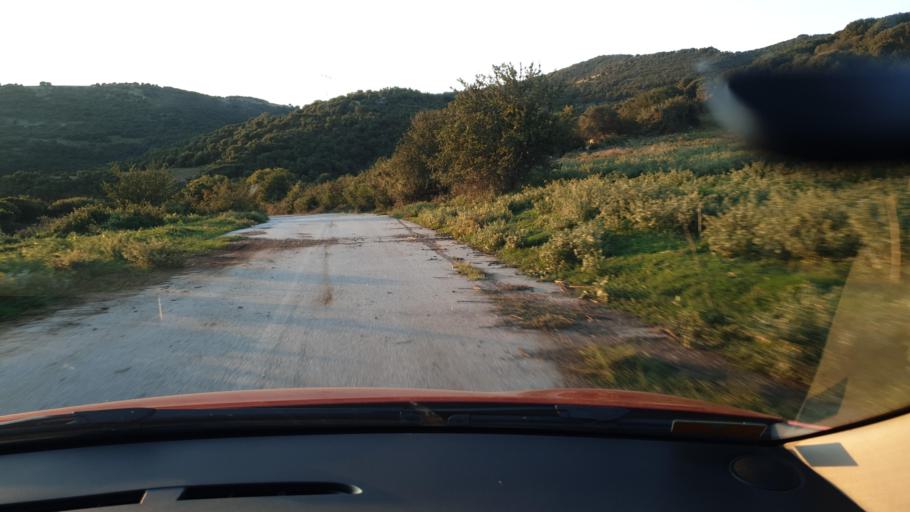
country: GR
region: Central Macedonia
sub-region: Nomos Chalkidikis
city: Galatista
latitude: 40.4576
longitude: 23.3112
